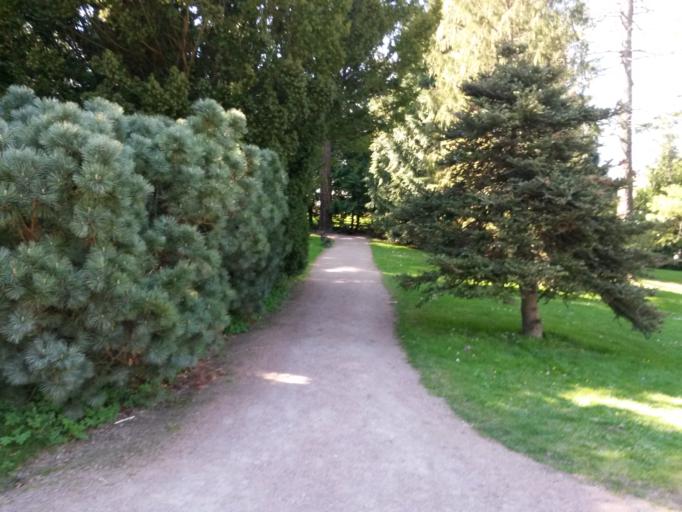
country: SE
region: Vaestra Goetaland
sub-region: Goteborg
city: Goeteborg
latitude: 57.6809
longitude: 11.9539
